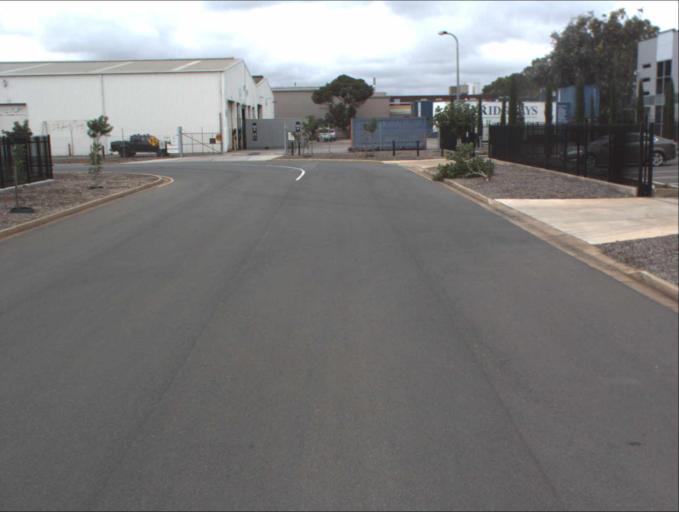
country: AU
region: South Australia
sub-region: Prospect
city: Prospect
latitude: -34.8795
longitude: 138.5793
